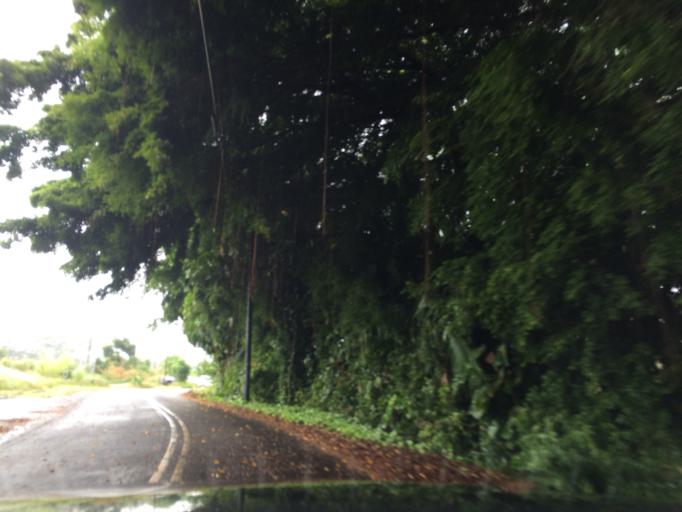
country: US
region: Hawaii
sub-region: Hawaii County
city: Hilo
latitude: 19.7185
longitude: -155.1095
